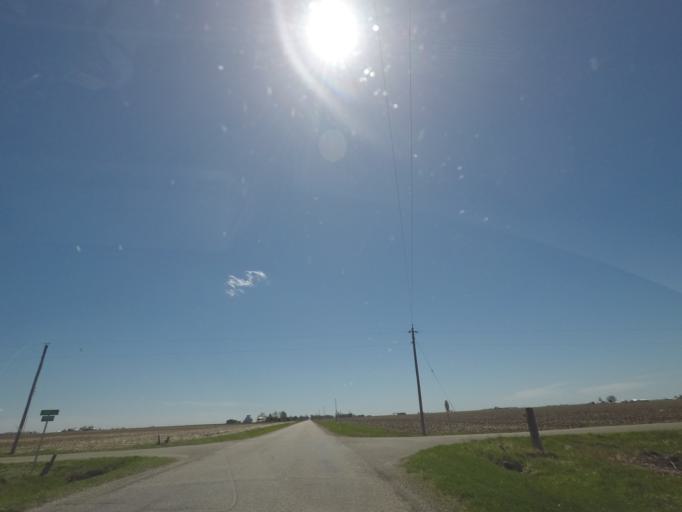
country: US
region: Illinois
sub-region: Logan County
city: Atlanta
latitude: 40.1650
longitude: -89.1936
